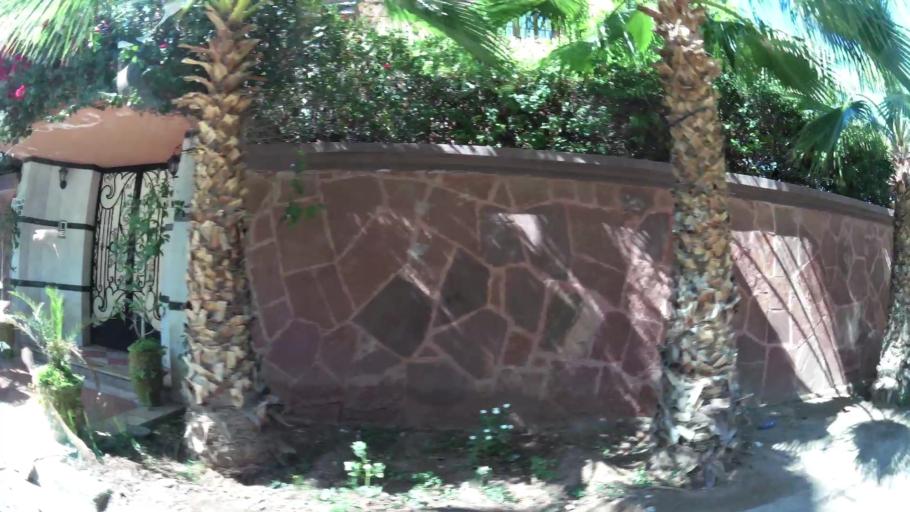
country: MA
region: Marrakech-Tensift-Al Haouz
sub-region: Marrakech
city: Marrakesh
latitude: 31.6442
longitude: -8.0464
